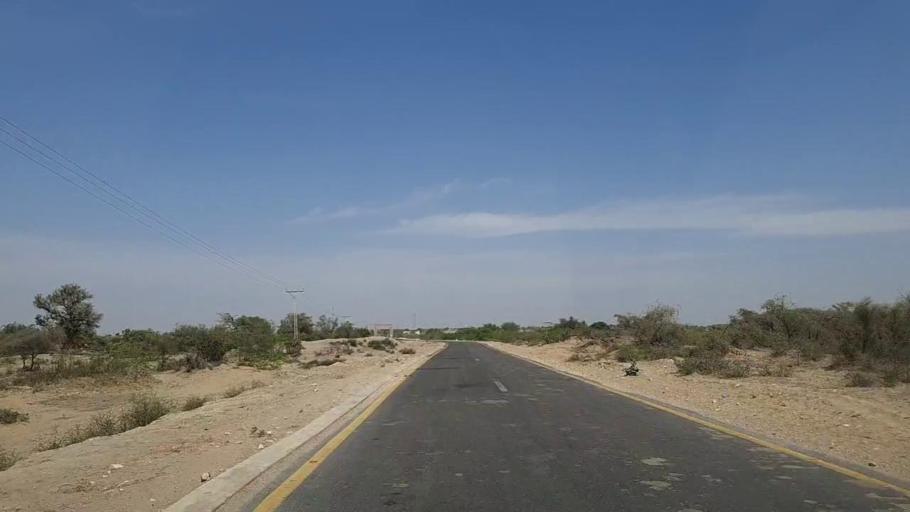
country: PK
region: Sindh
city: Mithi
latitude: 24.9647
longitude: 69.9111
